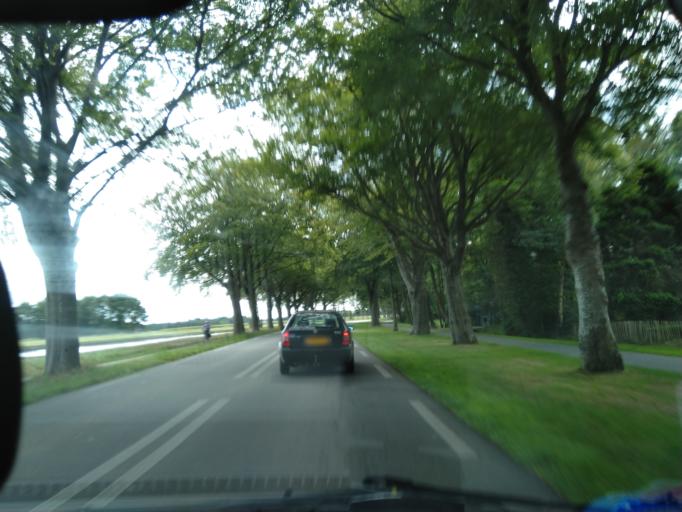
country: NL
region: Drenthe
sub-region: Gemeente Tynaarlo
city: Tynaarlo
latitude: 53.1063
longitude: 6.6045
